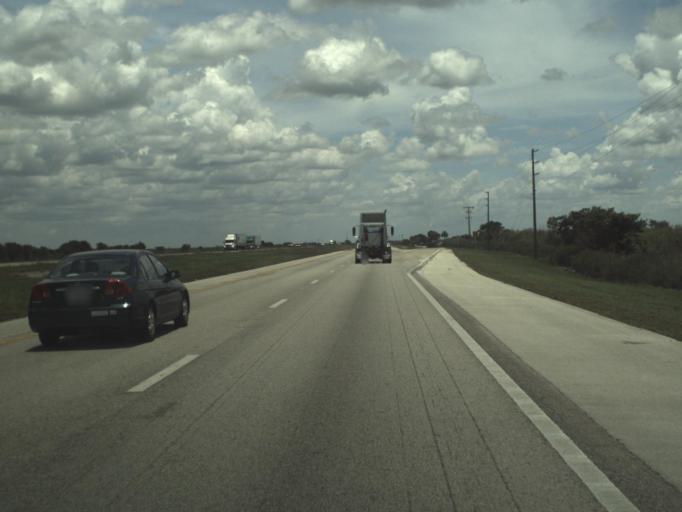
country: US
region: Florida
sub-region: Broward County
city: Weston
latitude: 26.1498
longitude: -80.7225
